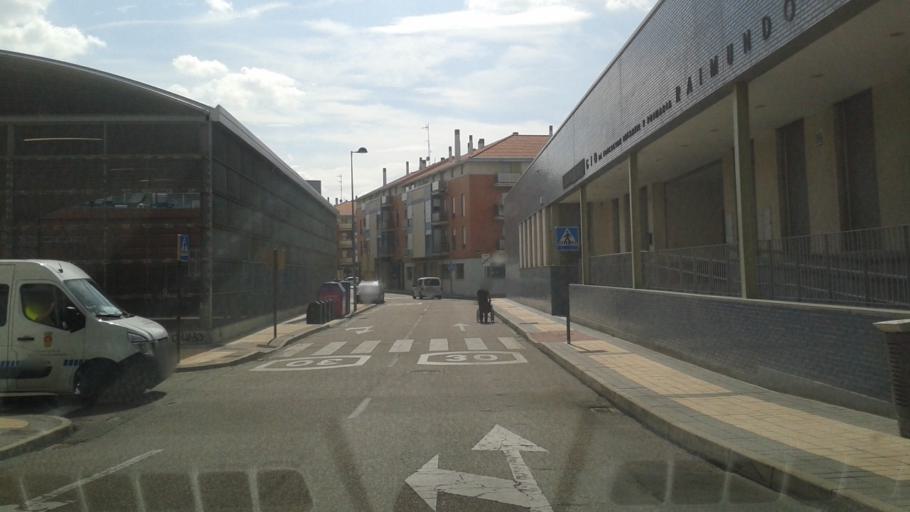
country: ES
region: Castille and Leon
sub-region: Provincia de Valladolid
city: Arroyo
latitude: 41.6265
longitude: -4.7757
